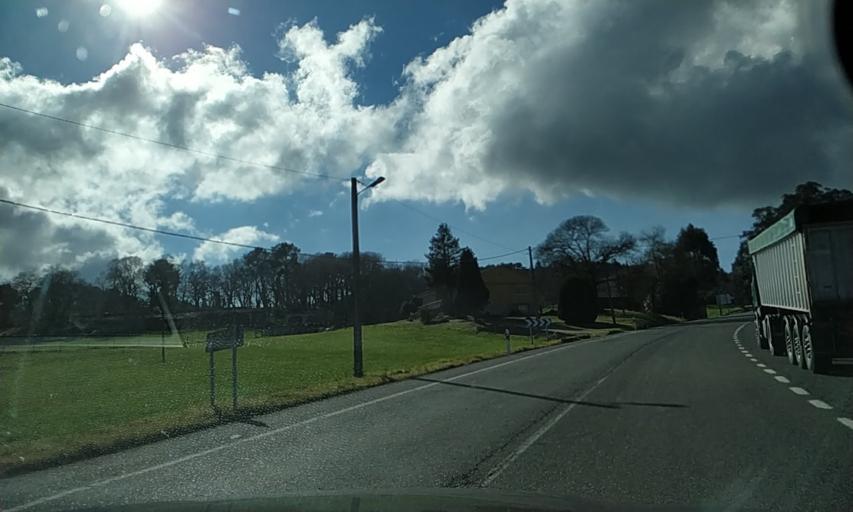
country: ES
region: Galicia
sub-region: Provincia de Pontevedra
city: Silleda
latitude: 42.6987
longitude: -8.3198
